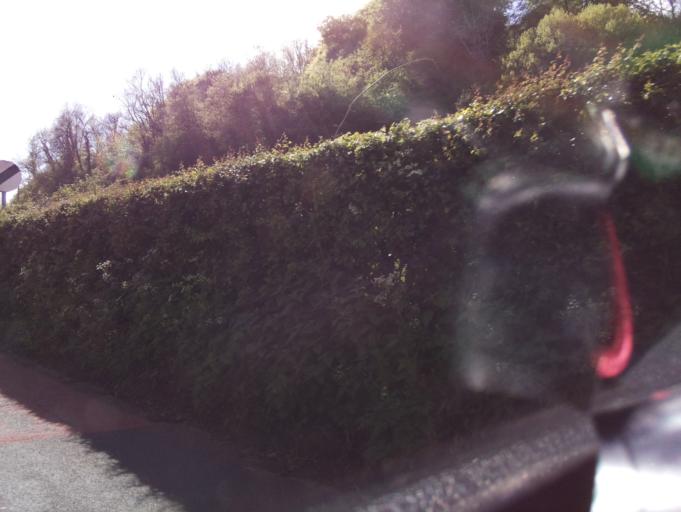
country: GB
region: Wales
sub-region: Caerphilly County Borough
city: Machen
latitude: 51.5781
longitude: -3.1287
